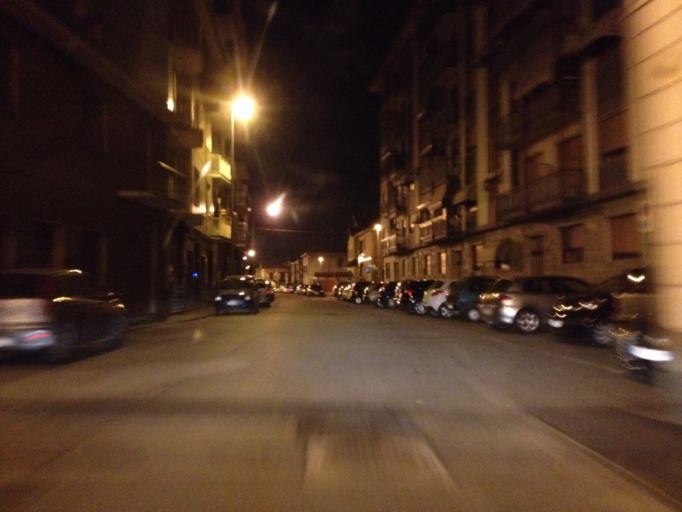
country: IT
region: Piedmont
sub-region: Provincia di Torino
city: Settimo Torinese
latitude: 45.1353
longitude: 7.7616
